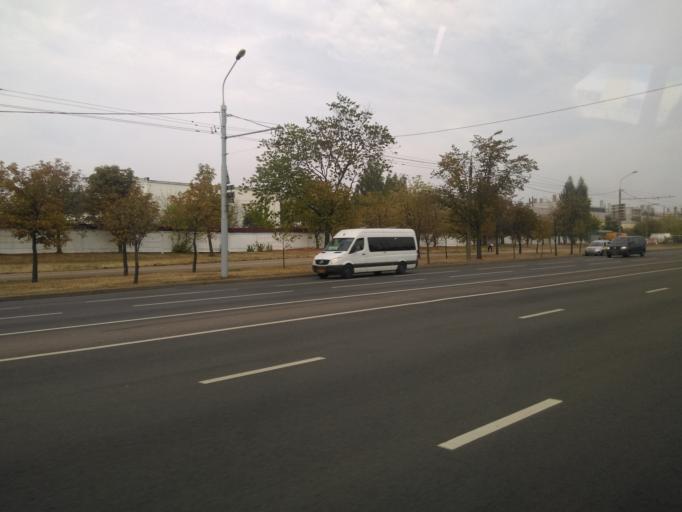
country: BY
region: Minsk
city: Minsk
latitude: 53.8956
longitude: 27.6430
